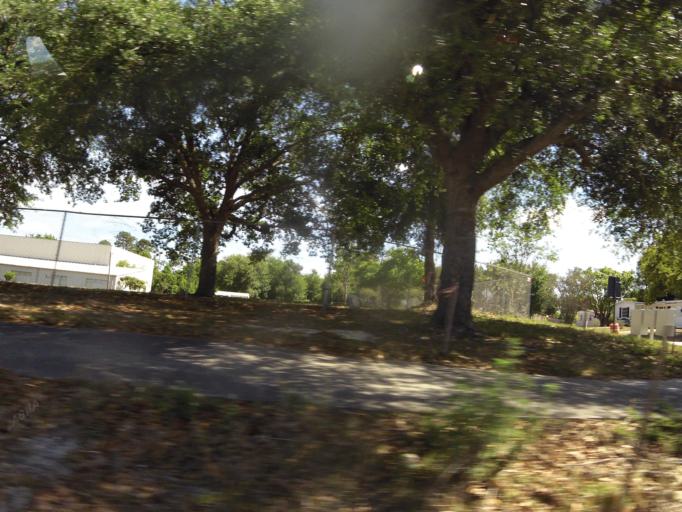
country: US
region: Florida
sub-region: Volusia County
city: Lake Helen
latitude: 28.9283
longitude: -81.1947
